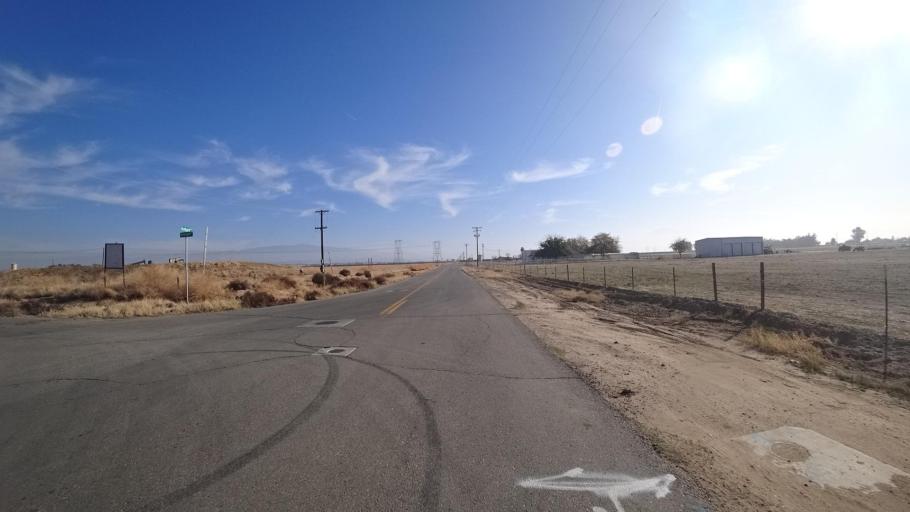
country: US
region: California
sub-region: Kern County
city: Lamont
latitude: 35.3399
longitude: -118.9055
